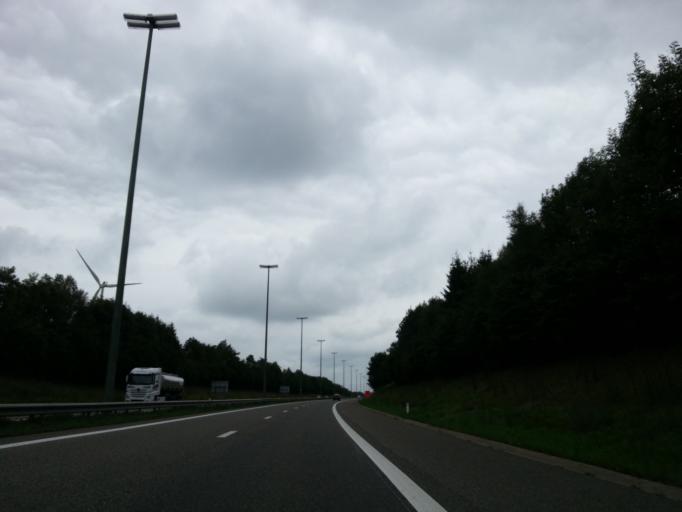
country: BE
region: Wallonia
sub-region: Province de Liege
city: Saint-Vith
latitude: 50.3061
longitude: 6.0794
